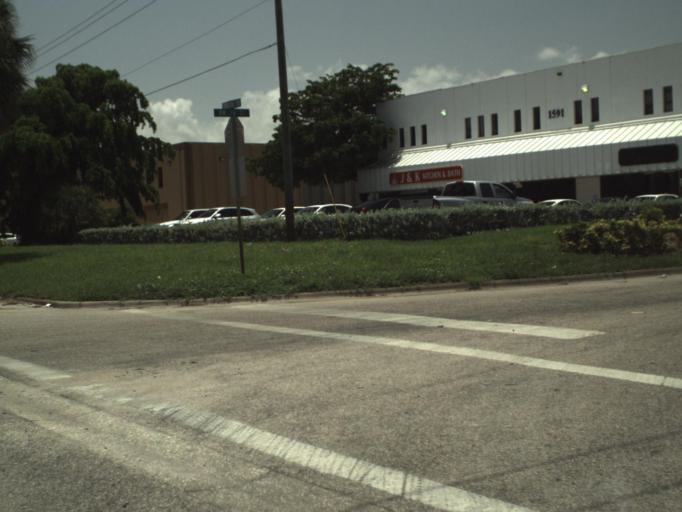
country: US
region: Florida
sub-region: Broward County
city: Coconut Creek
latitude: 26.2492
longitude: -80.1518
